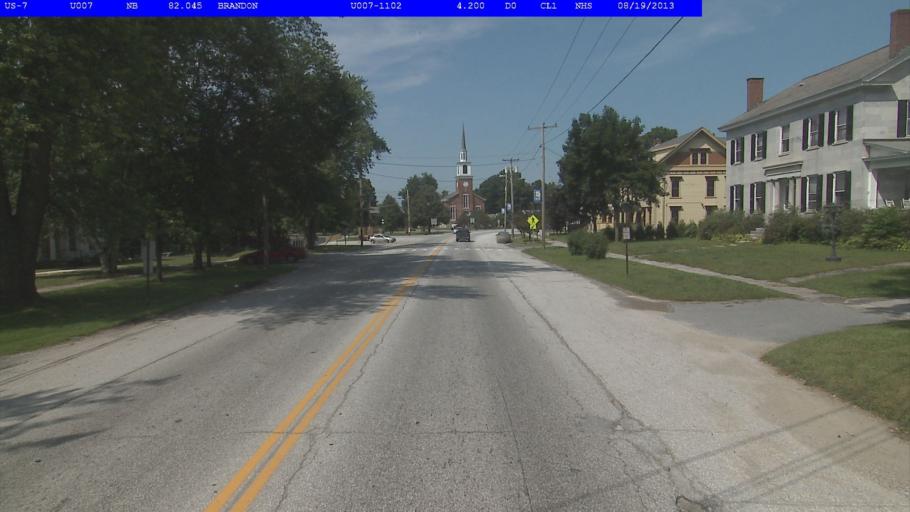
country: US
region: Vermont
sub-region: Rutland County
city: Brandon
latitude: 43.7999
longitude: -73.0915
